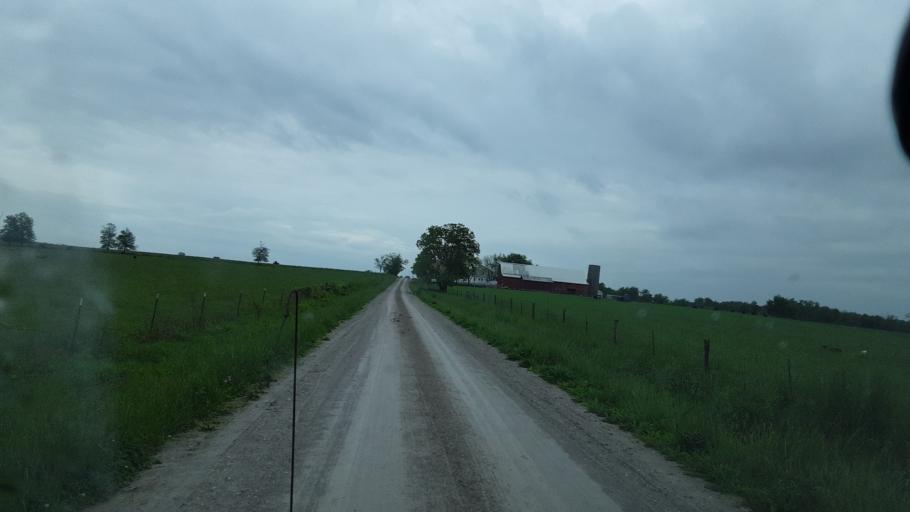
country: US
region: Missouri
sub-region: Randolph County
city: Moberly
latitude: 39.3139
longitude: -92.3050
